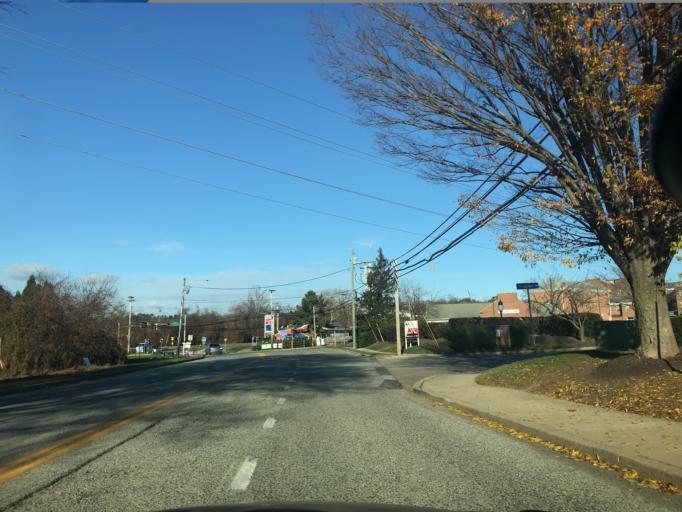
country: US
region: Maryland
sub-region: Baltimore County
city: Mays Chapel
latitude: 39.4182
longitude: -76.6678
